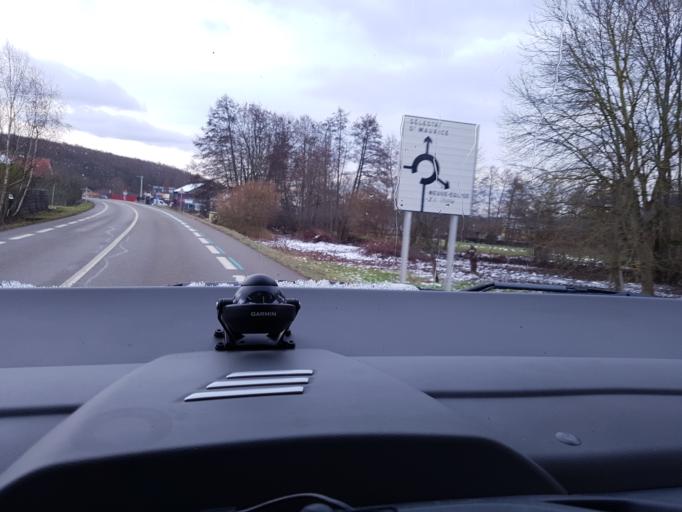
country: FR
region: Alsace
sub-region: Departement du Bas-Rhin
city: Ville
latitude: 48.3376
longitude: 7.3220
